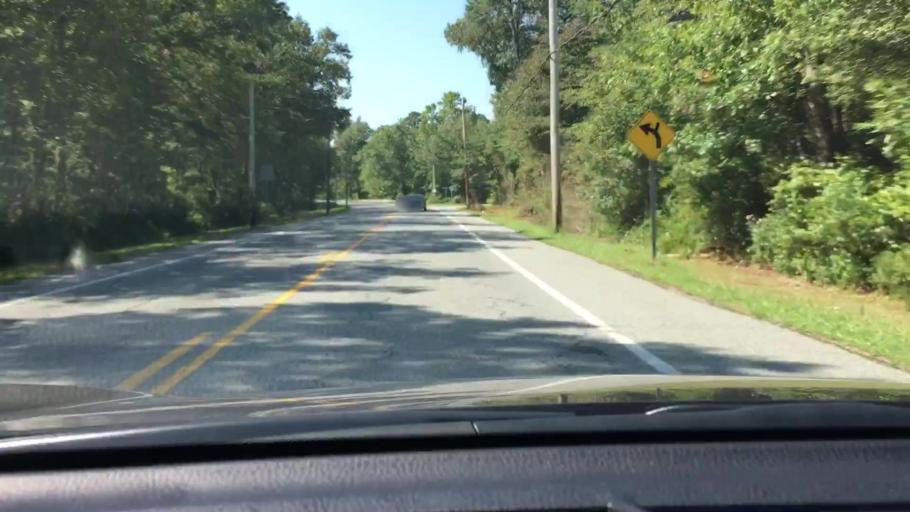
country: US
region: New Jersey
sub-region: Cape May County
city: Woodbine
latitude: 39.2868
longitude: -74.7902
